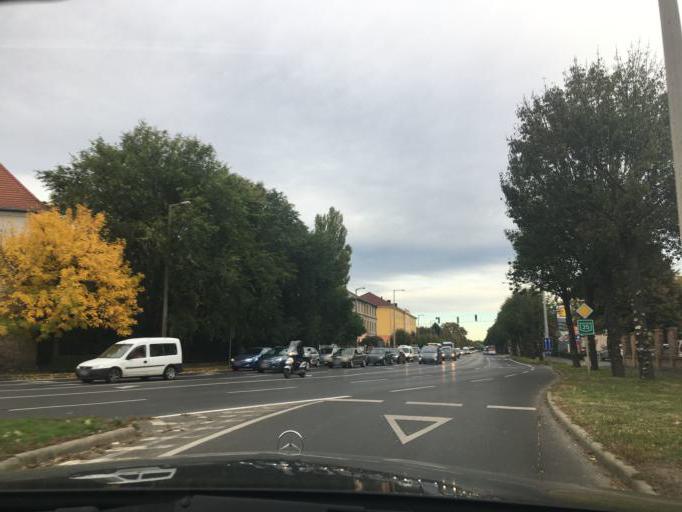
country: HU
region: Hajdu-Bihar
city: Debrecen
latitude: 47.5345
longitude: 21.6124
